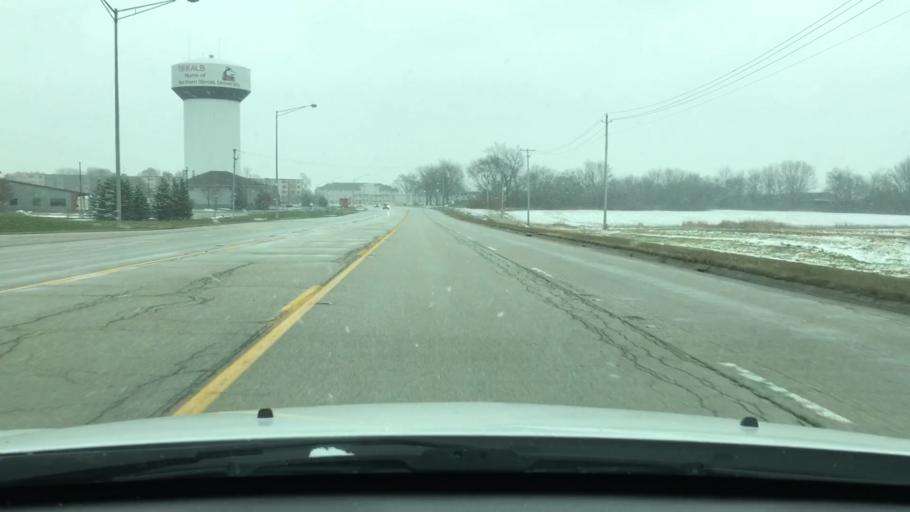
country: US
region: Illinois
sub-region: DeKalb County
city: DeKalb
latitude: 41.9318
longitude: -88.7856
